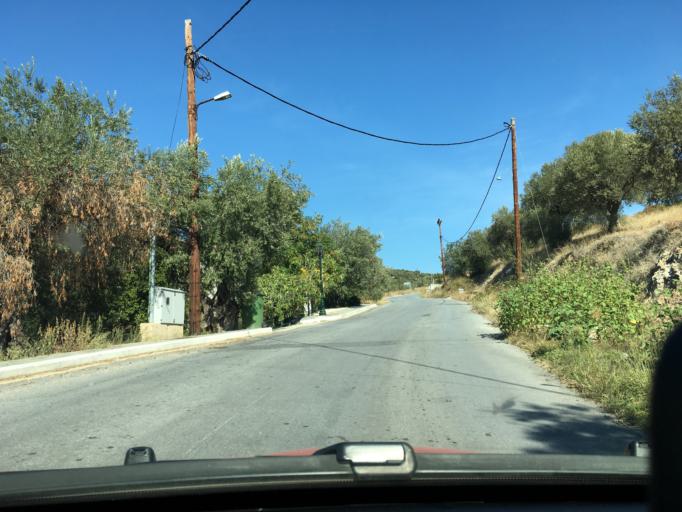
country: GR
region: Central Macedonia
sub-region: Nomos Chalkidikis
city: Agios Nikolaos
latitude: 40.3376
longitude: 23.7200
